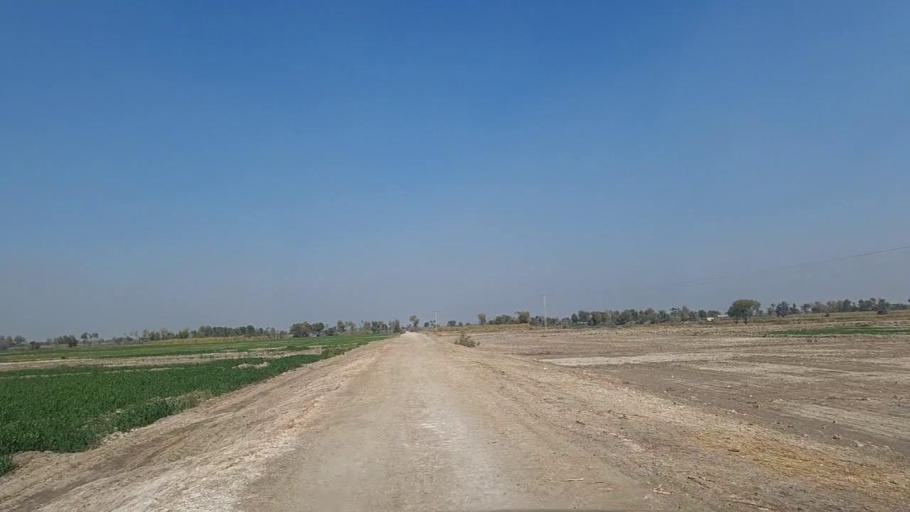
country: PK
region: Sindh
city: Daur
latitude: 26.4845
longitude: 68.3384
